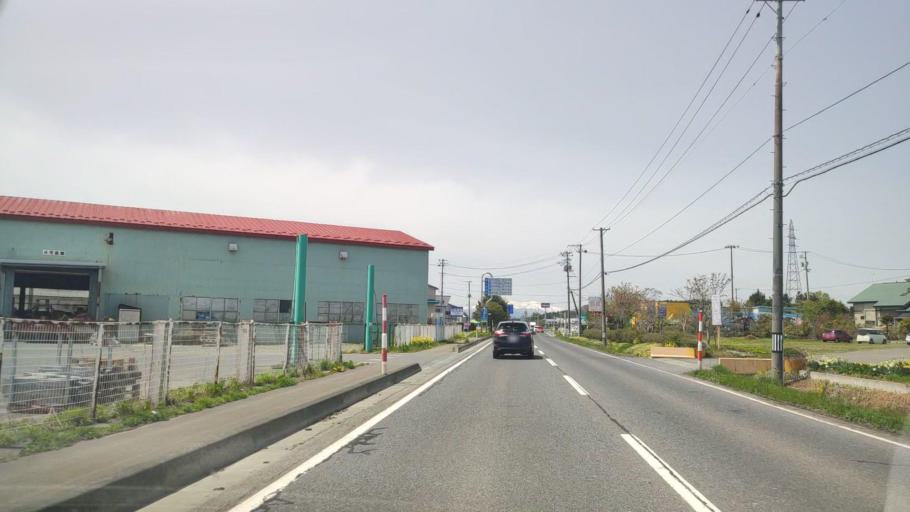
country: JP
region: Aomori
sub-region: Misawa Shi
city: Inuotose
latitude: 40.6119
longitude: 141.2643
